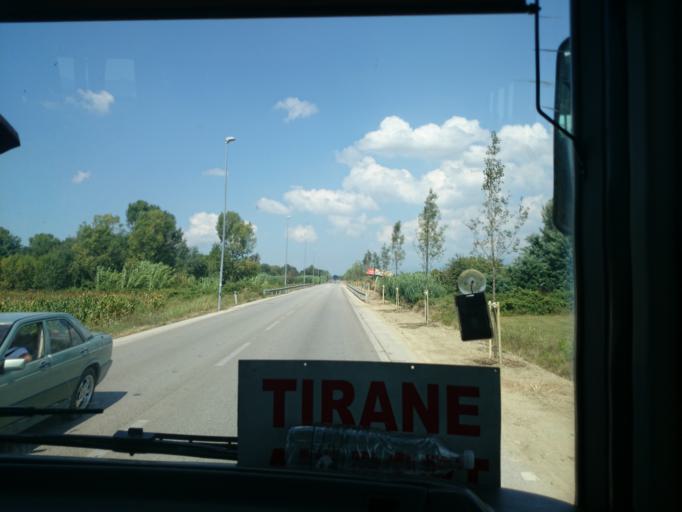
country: AL
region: Tirane
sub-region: Rrethi i Tiranes
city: Berxull
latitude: 41.3921
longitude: 19.7040
